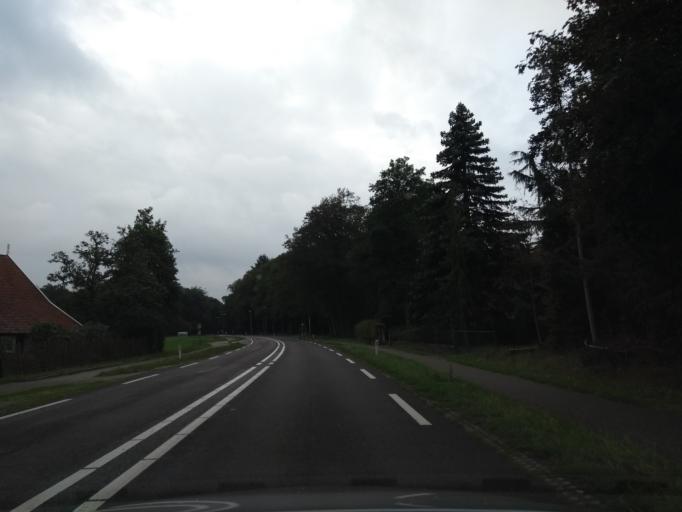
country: NL
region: Overijssel
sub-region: Gemeente Hof van Twente
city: Delden
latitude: 52.2854
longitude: 6.6711
